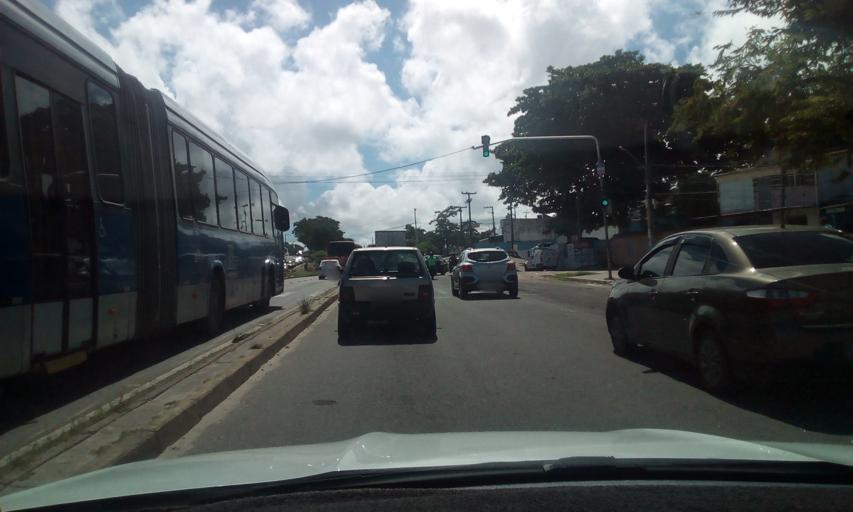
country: BR
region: Pernambuco
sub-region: Olinda
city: Olinda
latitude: -8.0083
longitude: -34.8580
